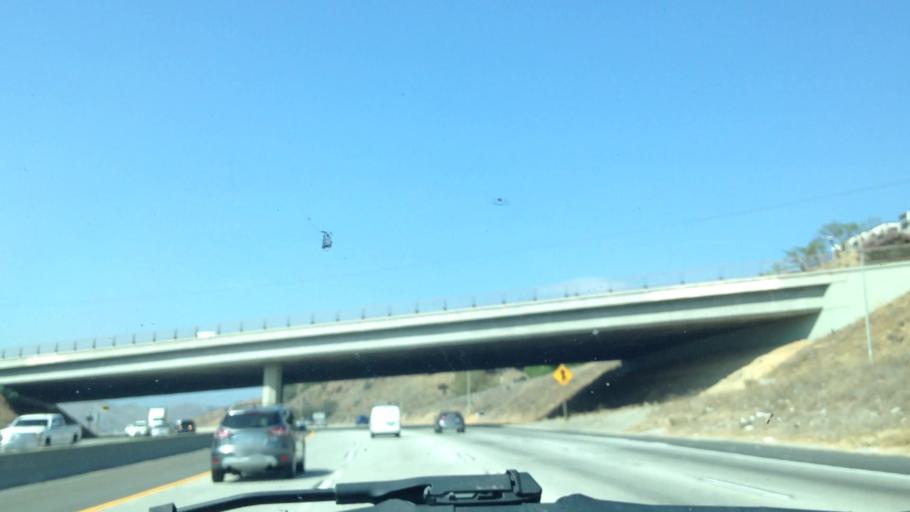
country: US
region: California
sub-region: Los Angeles County
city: Diamond Bar
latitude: 34.0425
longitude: -117.8011
